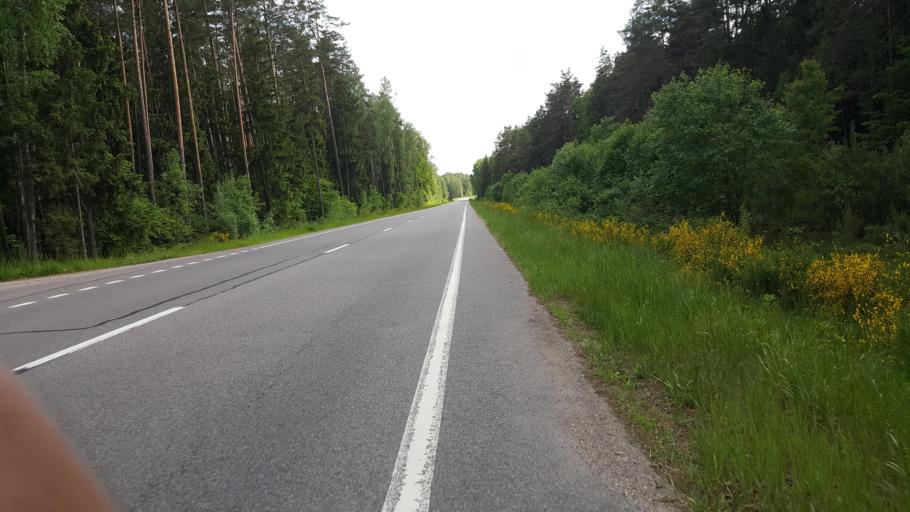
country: BY
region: Brest
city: Pruzhany
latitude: 52.5065
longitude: 24.1770
